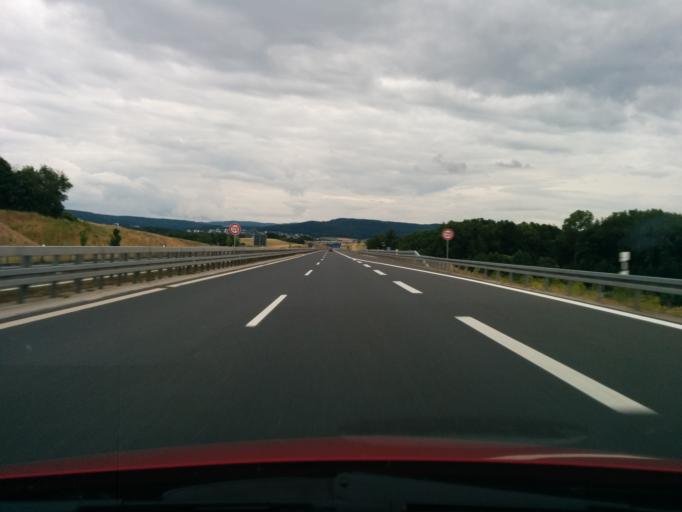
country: DE
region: Bavaria
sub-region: Upper Franconia
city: Lichtenfels
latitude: 50.1605
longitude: 11.0133
